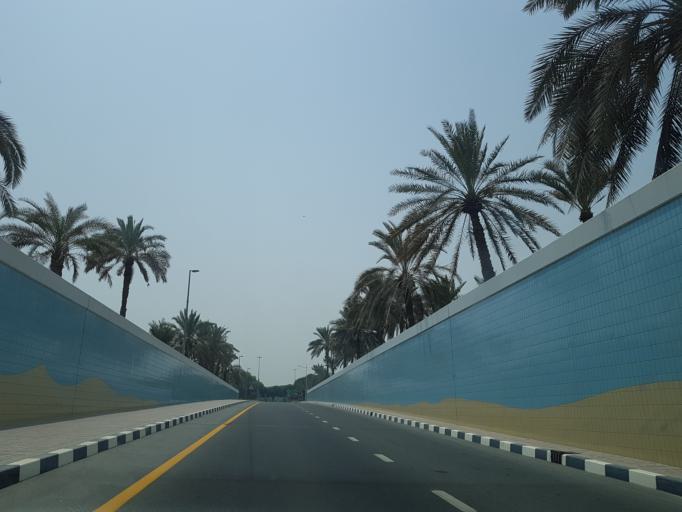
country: AE
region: Ash Shariqah
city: Sharjah
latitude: 25.2300
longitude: 55.2990
